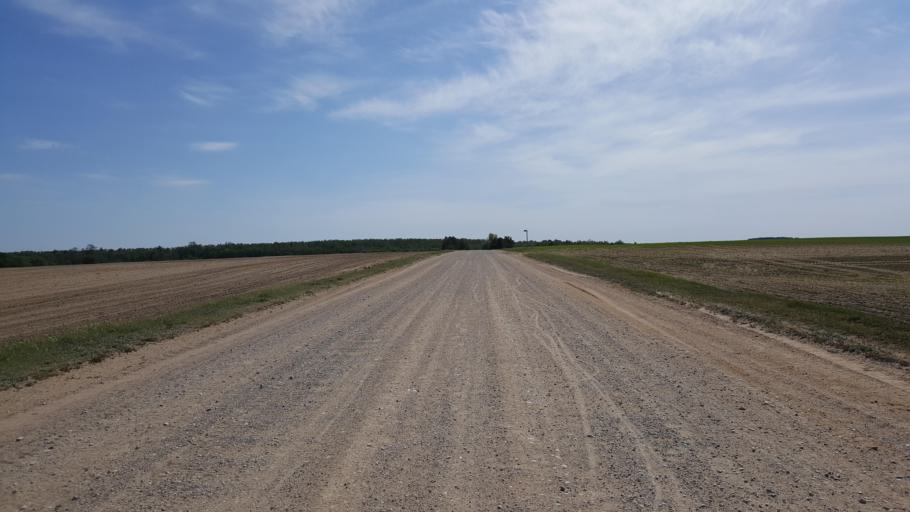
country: BY
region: Brest
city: Zhabinka
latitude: 52.3363
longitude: 24.0973
